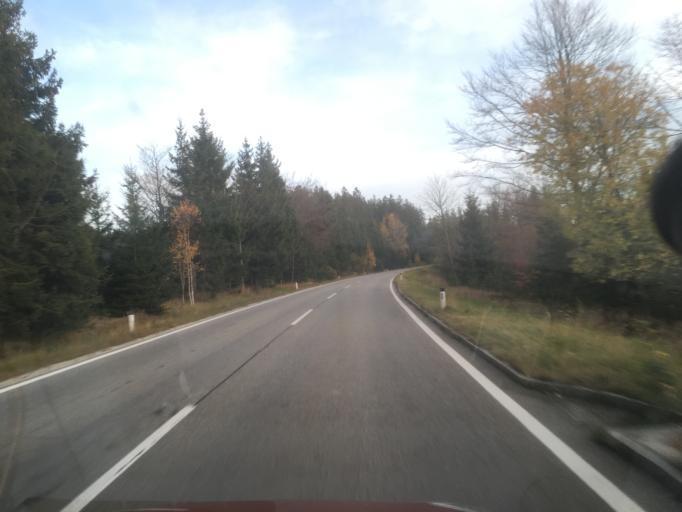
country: AT
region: Lower Austria
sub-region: Politischer Bezirk Zwettl
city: Langschlag
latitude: 48.5911
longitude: 14.7624
